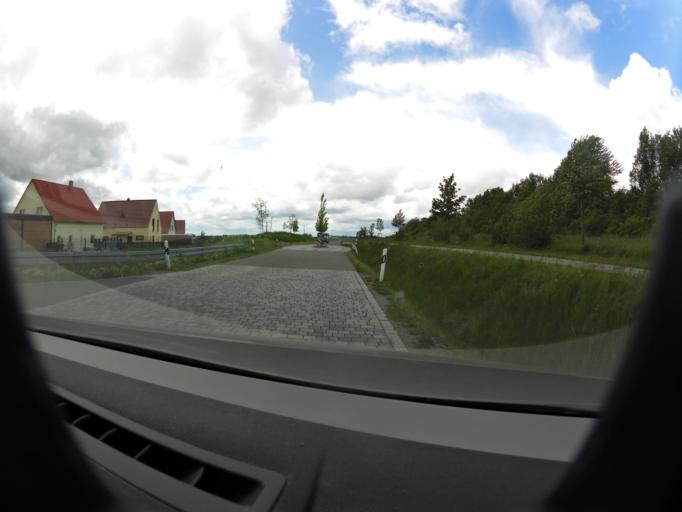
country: DE
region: Bavaria
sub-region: Regierungsbezirk Unterfranken
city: Iphofen
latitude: 49.7112
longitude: 10.2527
